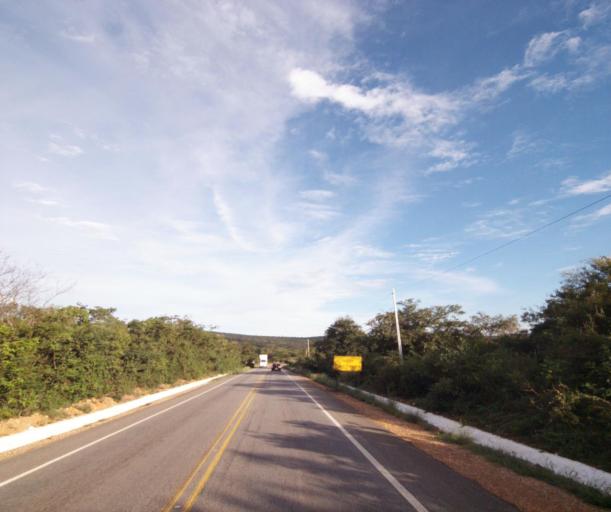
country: BR
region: Bahia
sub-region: Caetite
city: Caetite
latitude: -14.1285
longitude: -42.4139
